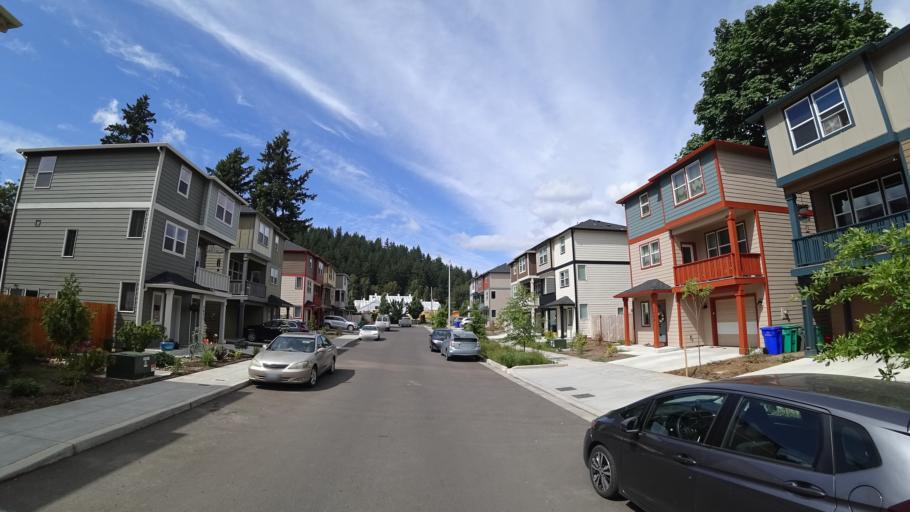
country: US
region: Oregon
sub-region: Multnomah County
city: Lents
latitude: 45.4953
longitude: -122.5533
